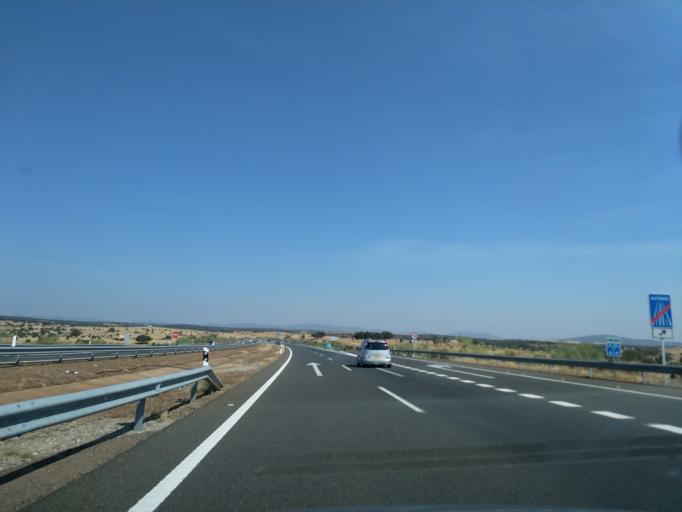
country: ES
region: Extremadura
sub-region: Provincia de Badajoz
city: Mirandilla
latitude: 38.9742
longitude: -6.3344
